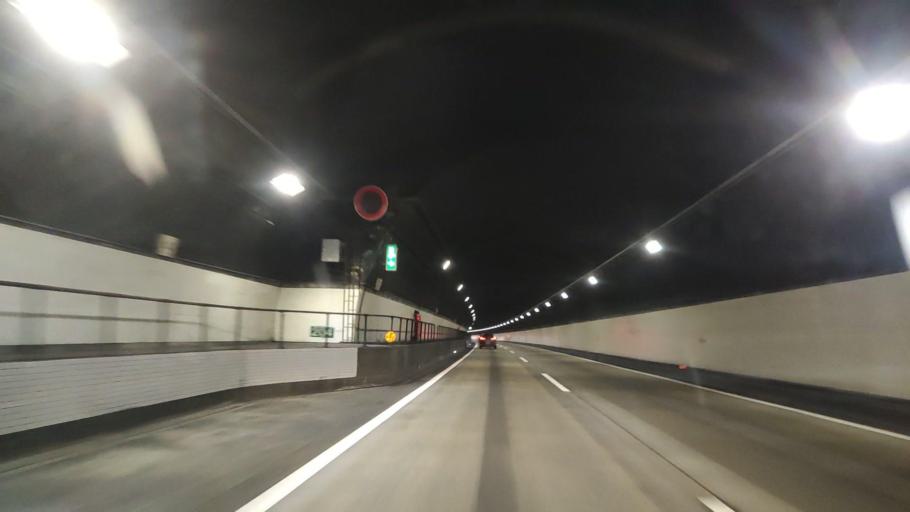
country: JP
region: Hiroshima
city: Shin'ichi
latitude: 34.4760
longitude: 133.2833
